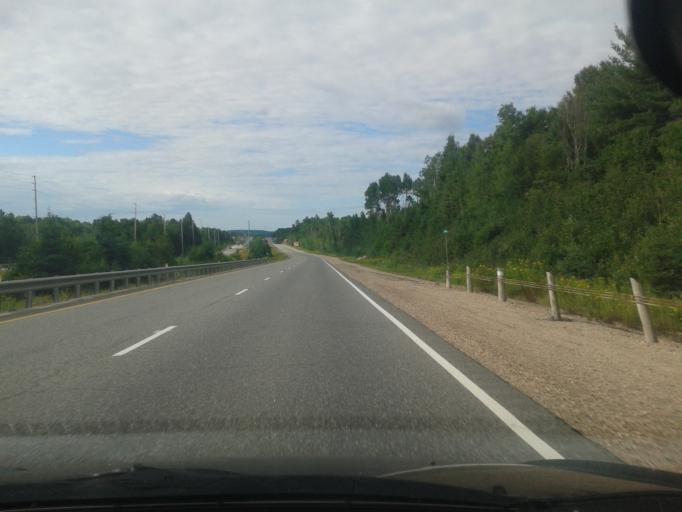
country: CA
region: Ontario
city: Powassan
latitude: 46.1211
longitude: -79.3642
